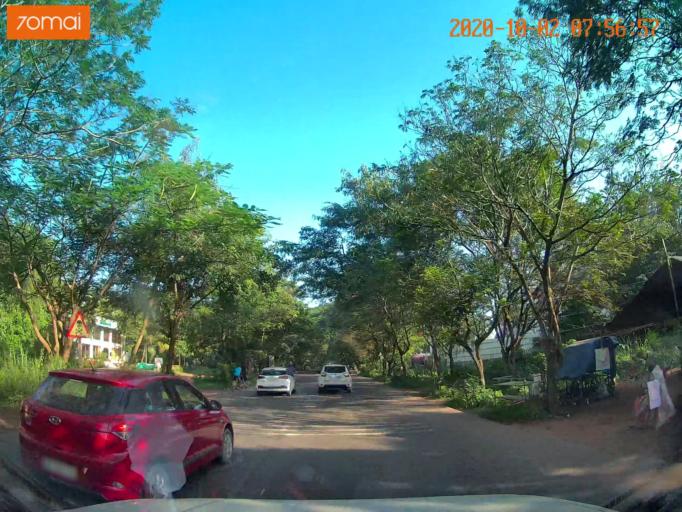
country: IN
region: Kerala
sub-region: Kozhikode
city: Ferokh
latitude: 11.1950
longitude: 75.8684
